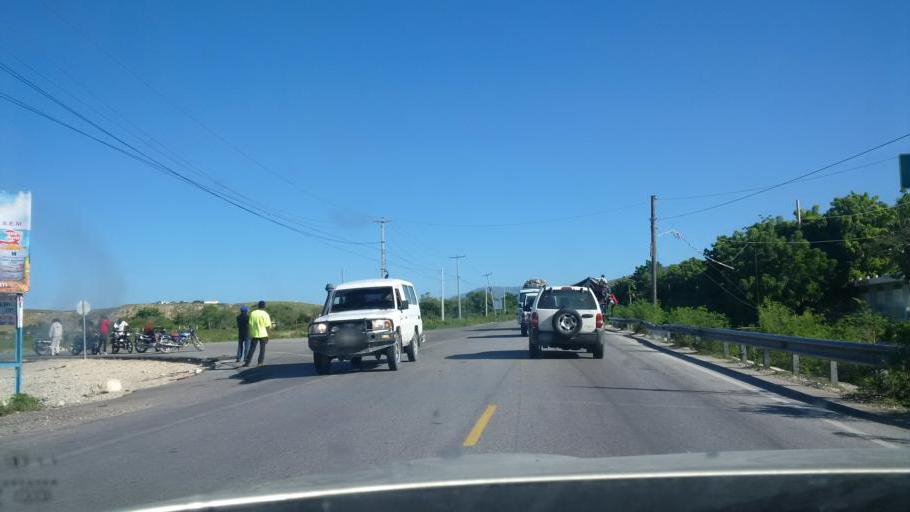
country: HT
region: Ouest
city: Cabaret
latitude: 18.7008
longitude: -72.3414
